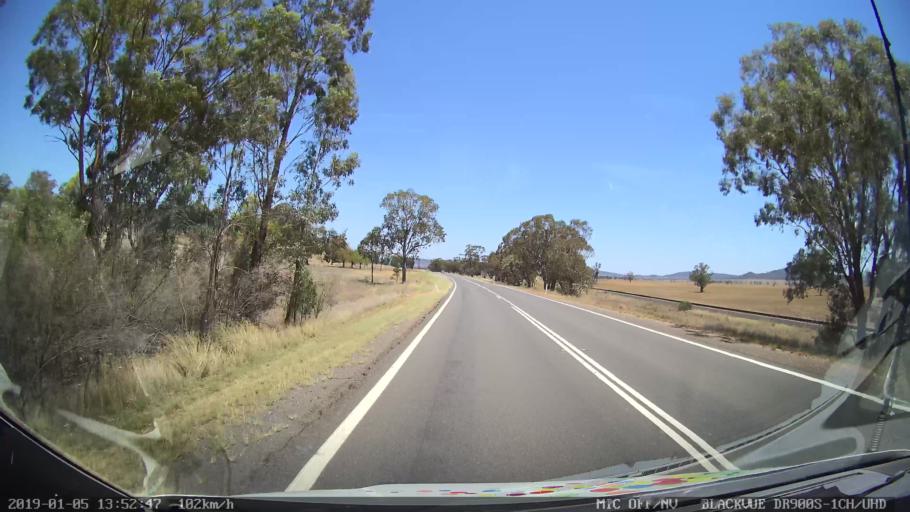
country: AU
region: New South Wales
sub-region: Gunnedah
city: Gunnedah
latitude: -31.0652
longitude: 150.2768
